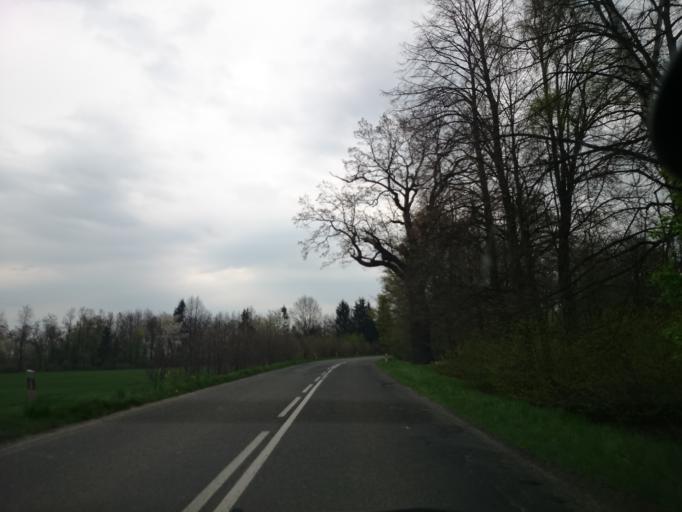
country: PL
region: Opole Voivodeship
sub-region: Powiat nyski
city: Glucholazy
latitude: 50.3643
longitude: 17.3724
